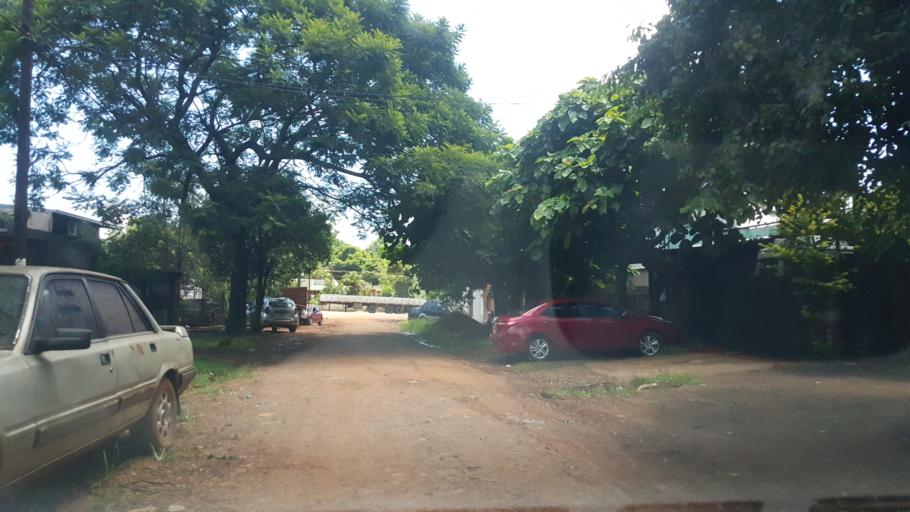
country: AR
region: Misiones
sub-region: Departamento de Capital
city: Posadas
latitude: -27.4107
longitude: -55.9091
